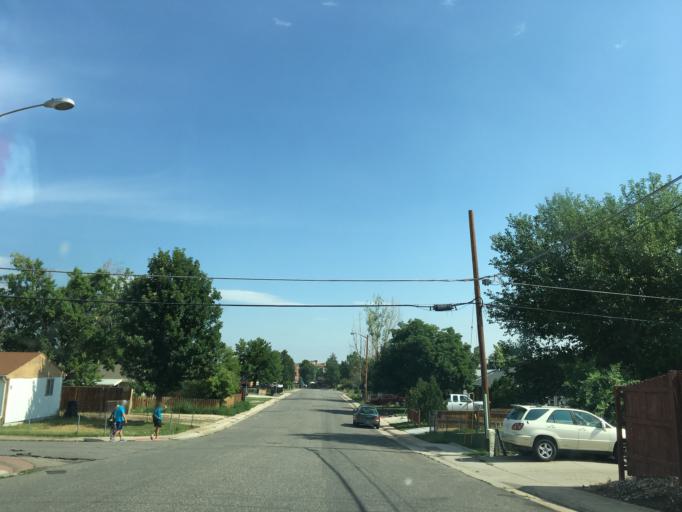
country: US
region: Colorado
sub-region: Jefferson County
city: Lakewood
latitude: 39.7008
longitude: -105.0424
